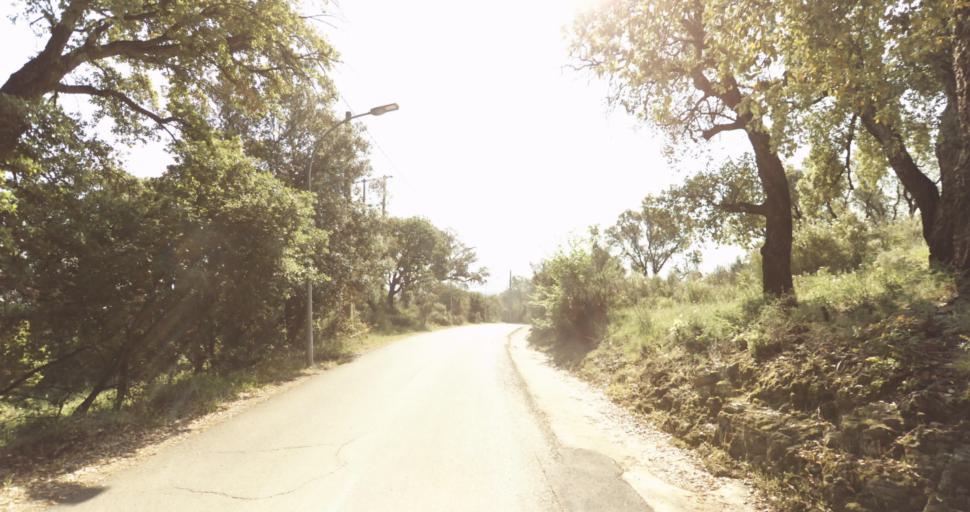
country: FR
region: Corsica
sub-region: Departement de la Haute-Corse
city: Biguglia
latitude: 42.6224
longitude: 9.4210
